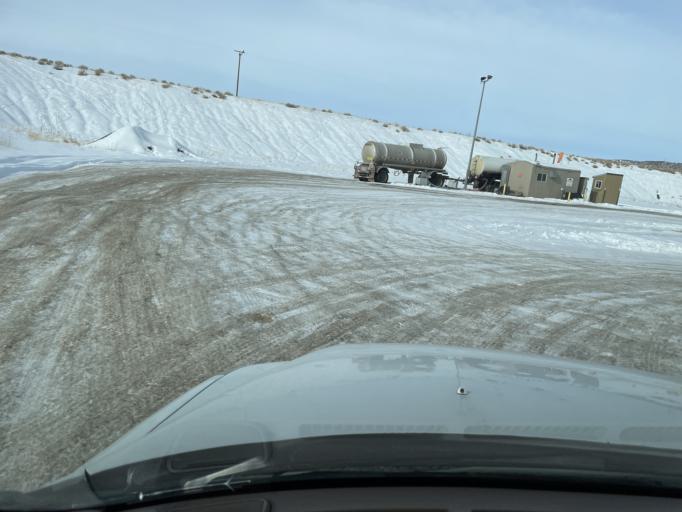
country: US
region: Colorado
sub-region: Moffat County
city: Craig
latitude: 40.3110
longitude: -107.6936
